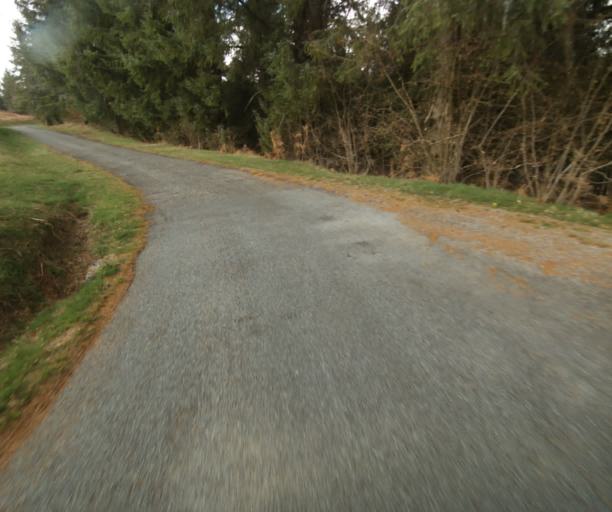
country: FR
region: Limousin
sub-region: Departement de la Correze
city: Egletons
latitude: 45.2725
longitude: 1.9981
